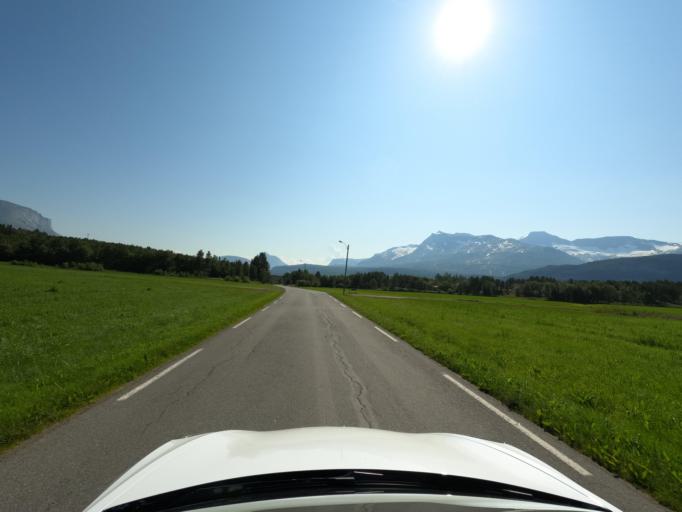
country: NO
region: Nordland
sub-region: Narvik
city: Narvik
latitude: 68.3218
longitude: 17.2894
